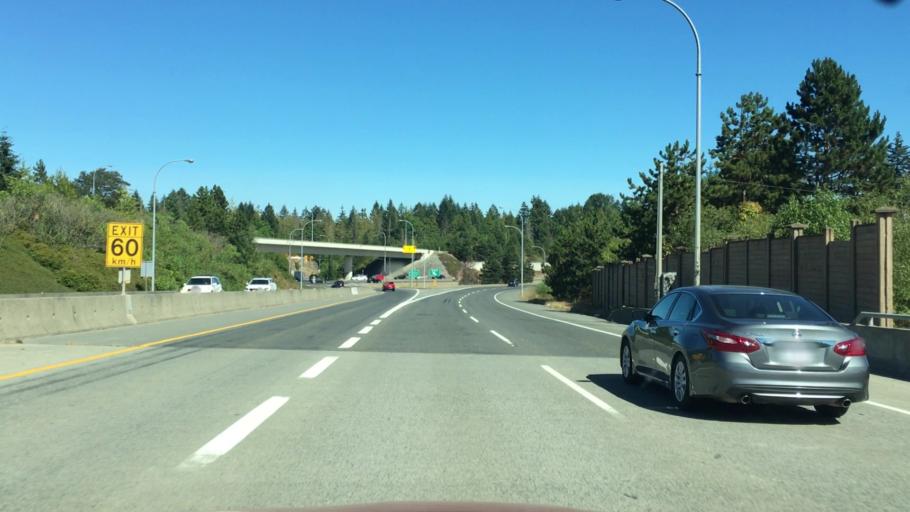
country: CA
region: British Columbia
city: Nanaimo
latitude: 49.1243
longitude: -123.9212
